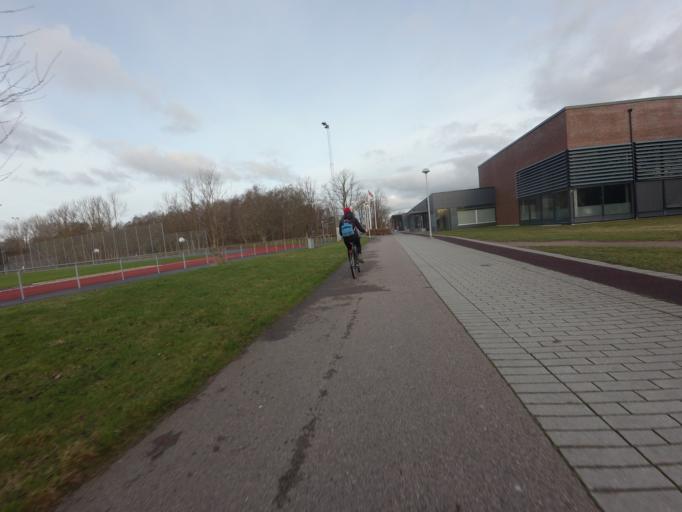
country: SE
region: Skane
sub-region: Hoganas Kommun
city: Hoganas
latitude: 56.1847
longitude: 12.5660
